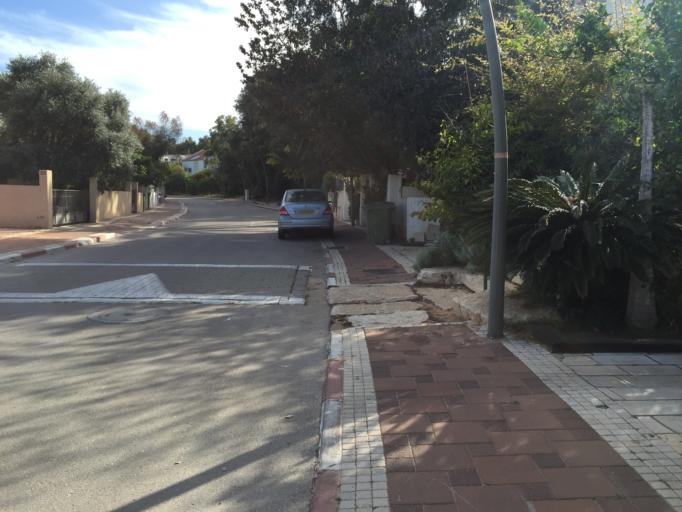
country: IL
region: Haifa
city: Qesarya
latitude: 32.5141
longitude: 34.9015
